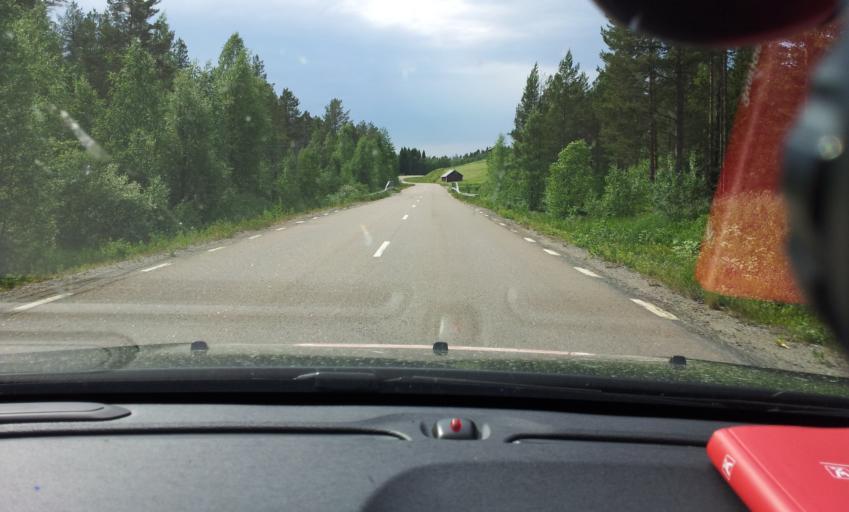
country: SE
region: Jaemtland
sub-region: OEstersunds Kommun
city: Brunflo
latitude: 62.6611
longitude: 14.8671
